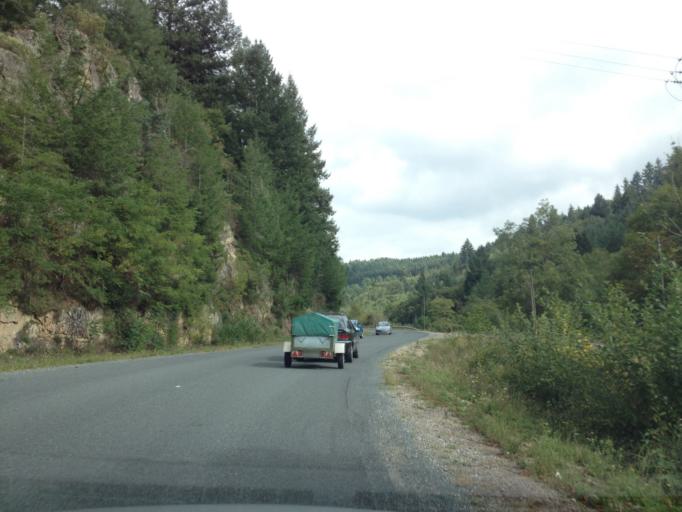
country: FR
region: Rhone-Alpes
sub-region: Departement de la Loire
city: Renaison
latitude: 46.0459
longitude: 3.8927
